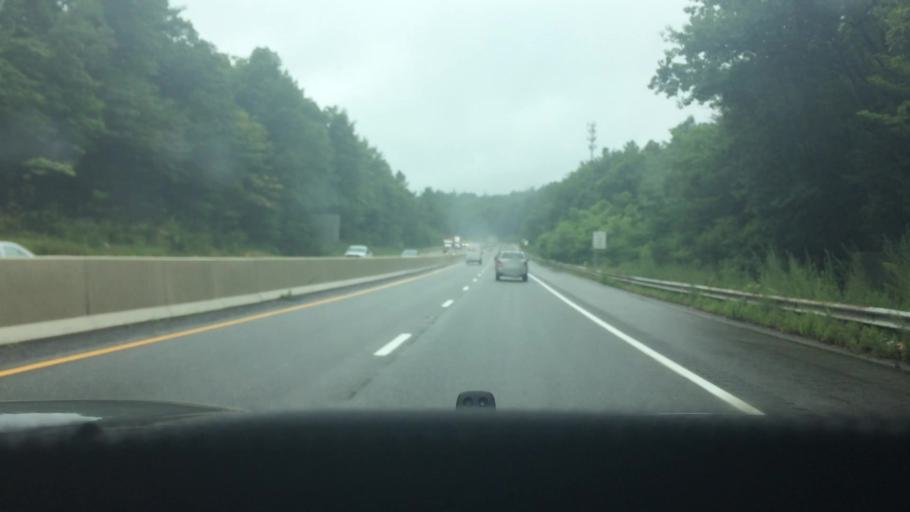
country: US
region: Massachusetts
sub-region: Worcester County
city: Fitchburg
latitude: 42.5519
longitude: -71.7920
